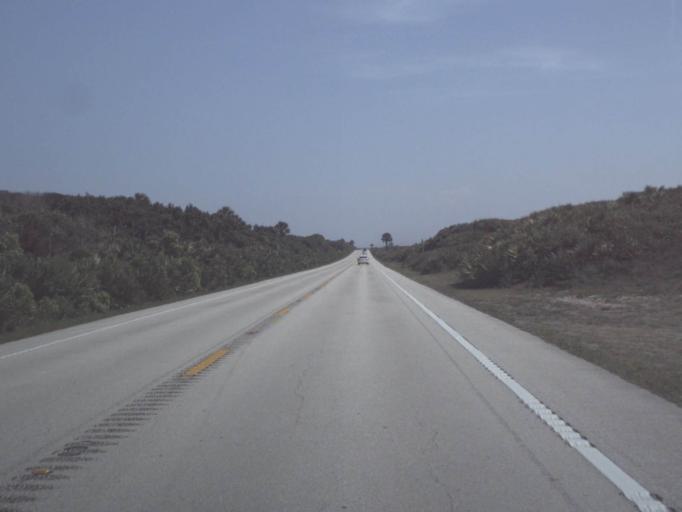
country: US
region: Florida
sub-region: Saint Johns County
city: Palm Valley
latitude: 30.1077
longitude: -81.3435
